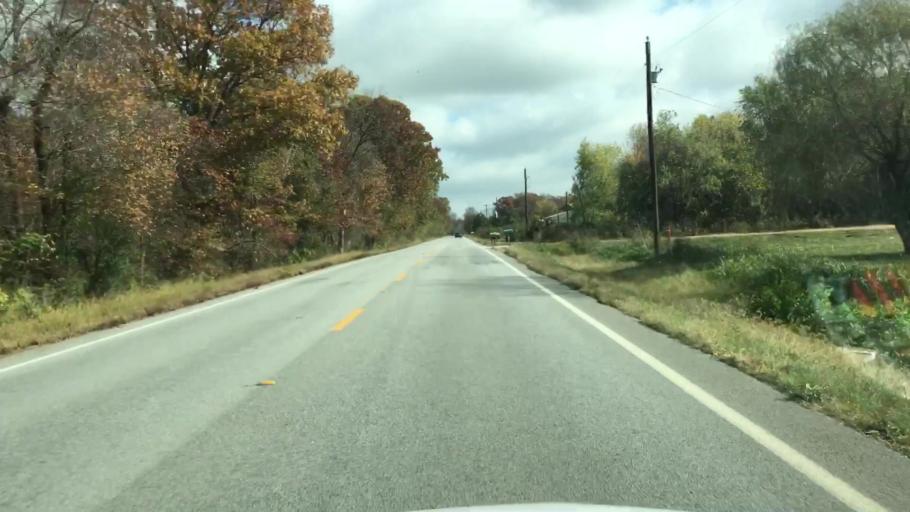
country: US
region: Arkansas
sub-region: Benton County
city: Gentry
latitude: 36.2578
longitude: -94.3906
